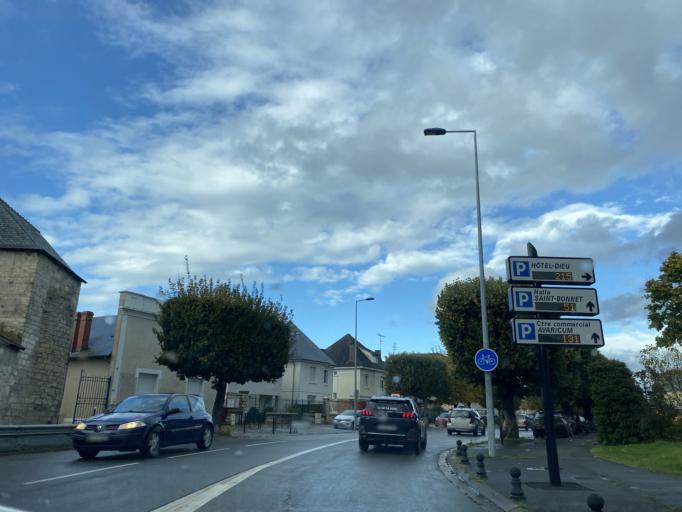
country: FR
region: Centre
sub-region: Departement du Cher
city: Bourges
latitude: 47.0871
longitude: 2.3887
